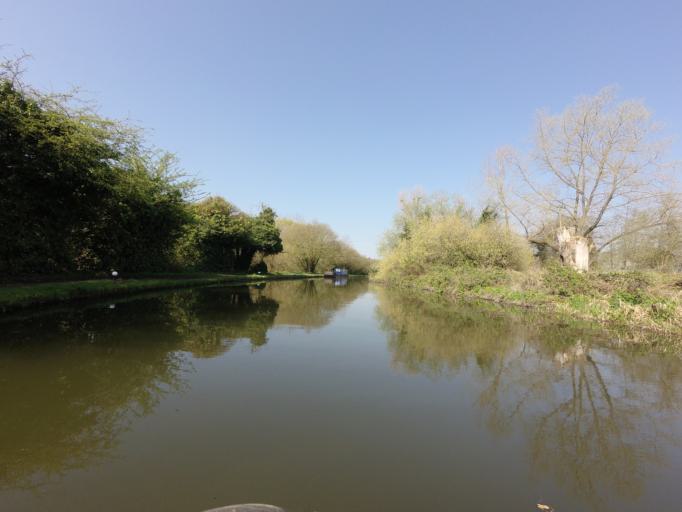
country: GB
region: England
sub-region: Hertfordshire
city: Bovingdon
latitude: 51.7508
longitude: -0.5346
